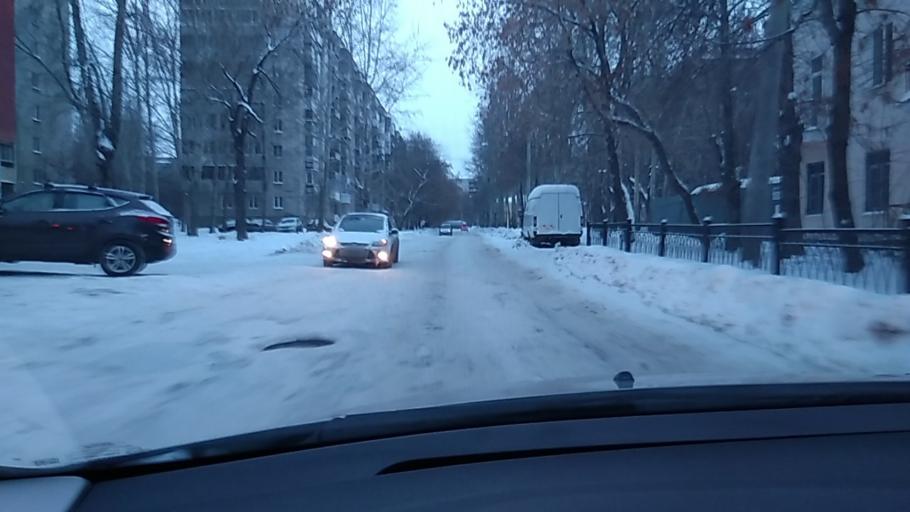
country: RU
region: Sverdlovsk
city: Yekaterinburg
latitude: 56.8955
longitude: 60.5995
